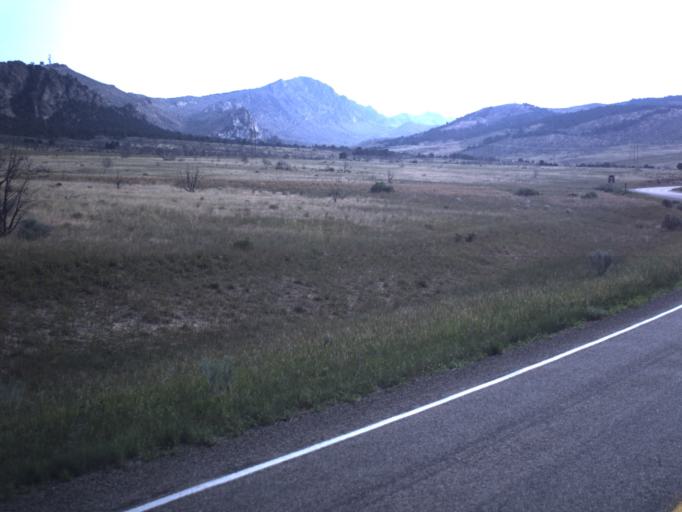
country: US
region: Utah
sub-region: Daggett County
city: Manila
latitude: 40.9450
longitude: -109.4344
